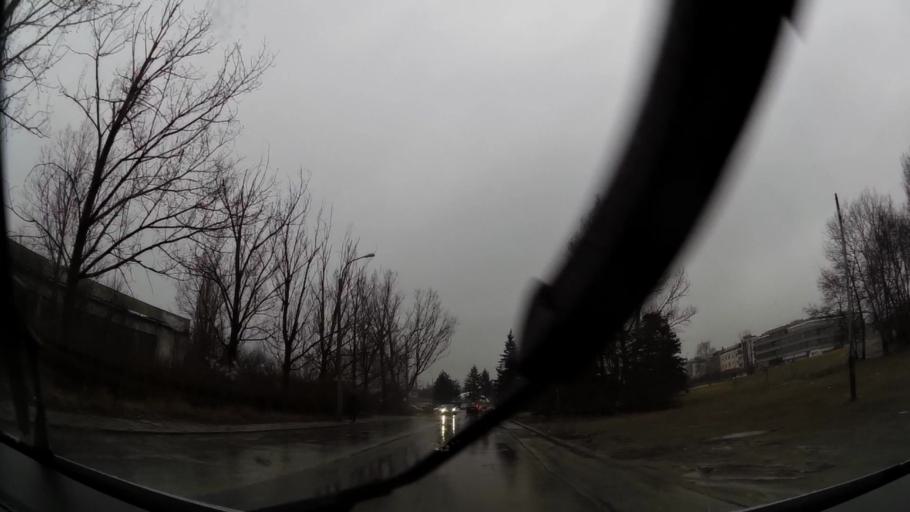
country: BG
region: Sofia-Capital
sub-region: Stolichna Obshtina
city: Sofia
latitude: 42.6526
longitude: 23.3534
